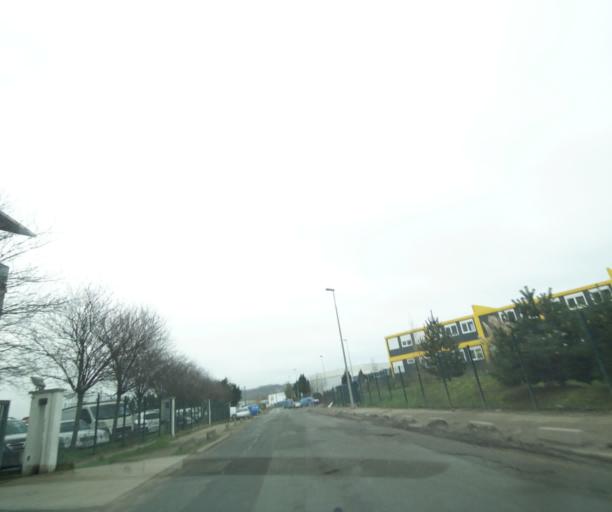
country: FR
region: Ile-de-France
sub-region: Departement du Val-de-Marne
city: Ablon-sur-Seine
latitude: 48.7317
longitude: 2.4324
